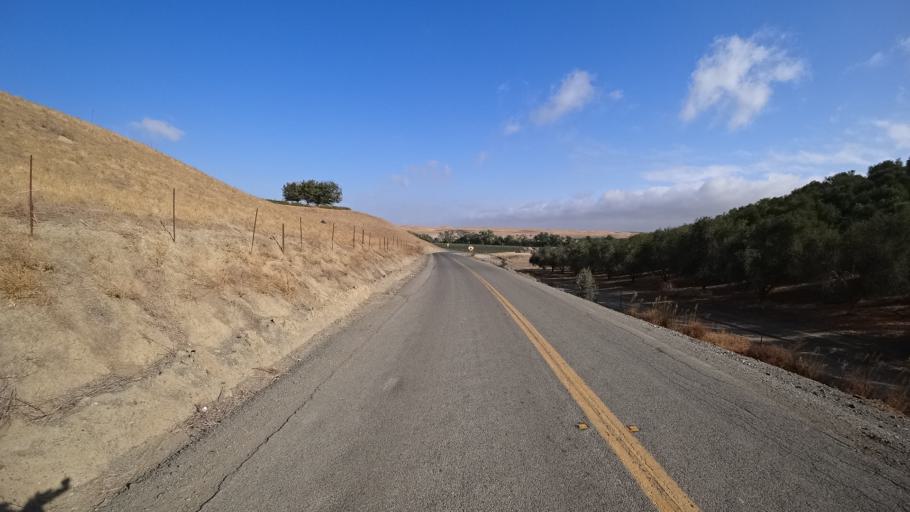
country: US
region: California
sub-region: Yolo County
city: Dunnigan
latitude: 38.8018
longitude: -122.0070
